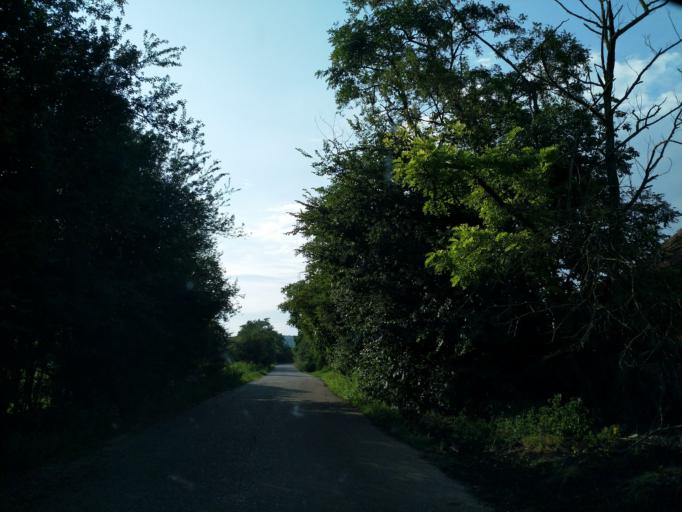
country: RS
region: Central Serbia
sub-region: Pomoravski Okrug
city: Jagodina
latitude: 44.0020
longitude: 21.1860
